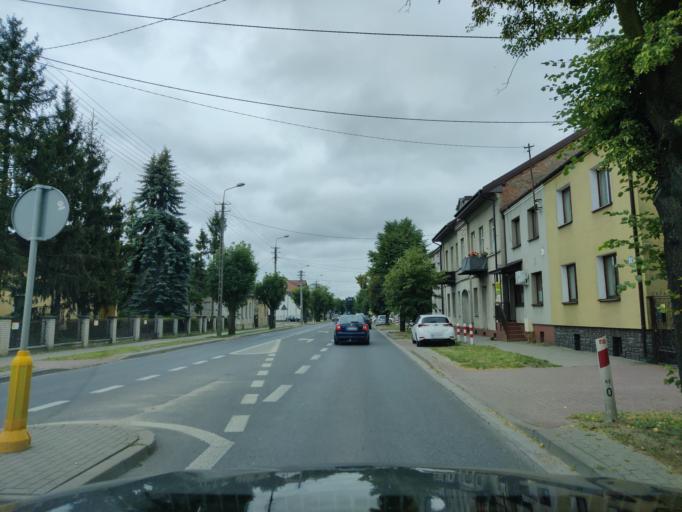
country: PL
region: Masovian Voivodeship
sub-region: Powiat pultuski
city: Pultusk
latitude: 52.7111
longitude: 21.0836
